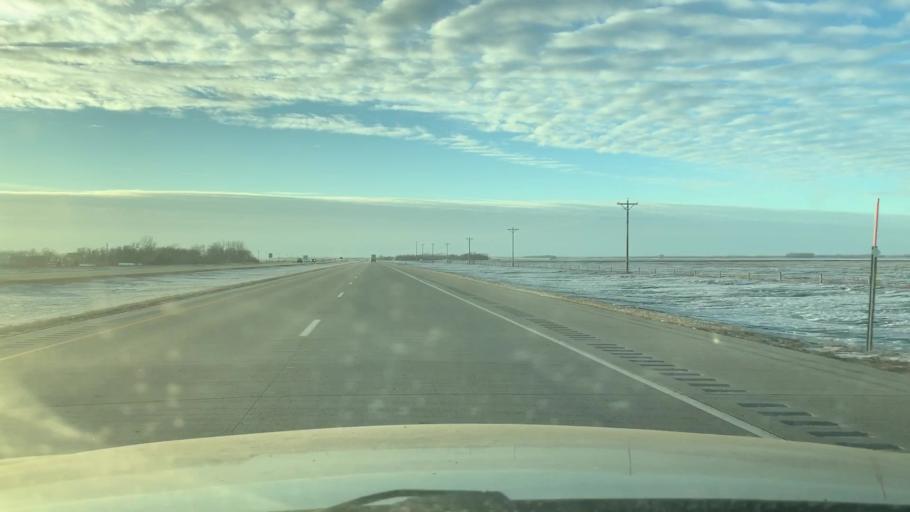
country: US
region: North Dakota
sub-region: Cass County
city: Casselton
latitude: 46.8760
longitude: -97.2967
